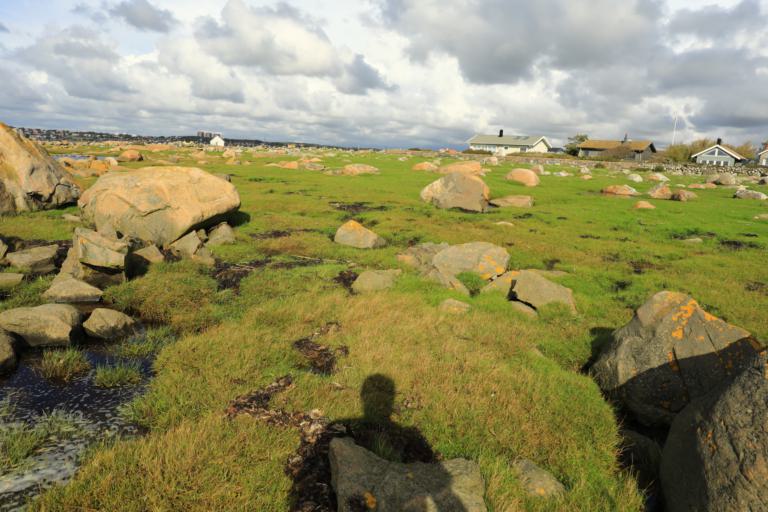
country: SE
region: Halland
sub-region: Varbergs Kommun
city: Traslovslage
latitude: 57.0686
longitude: 12.2525
